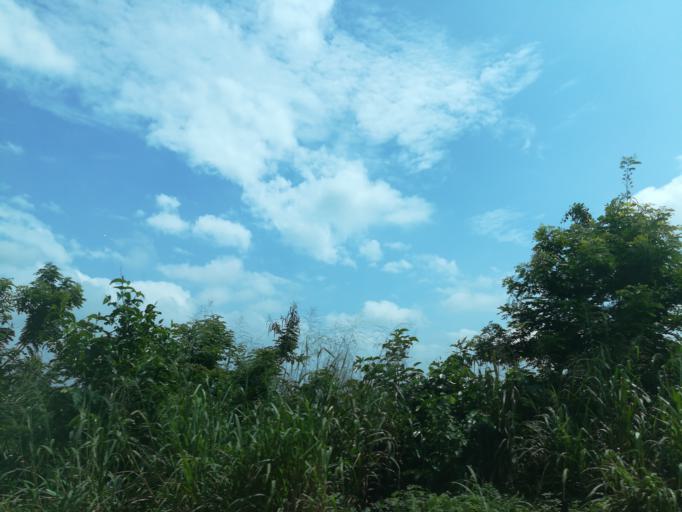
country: NG
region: Lagos
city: Ikorodu
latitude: 6.6554
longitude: 3.6914
